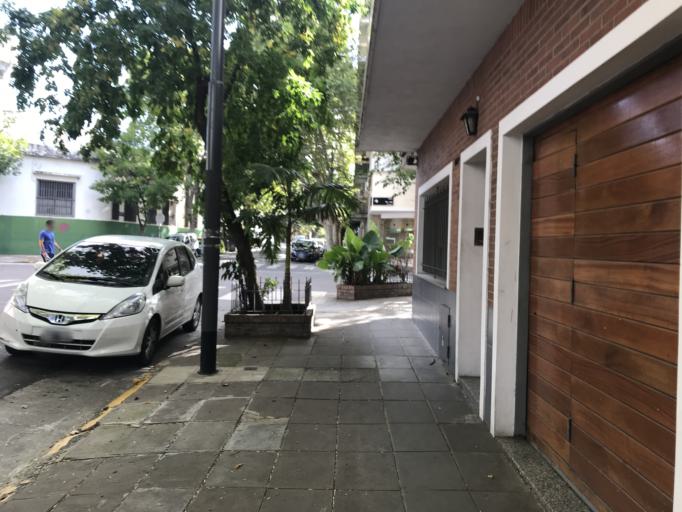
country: AR
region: Buenos Aires F.D.
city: Villa Santa Rita
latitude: -34.6309
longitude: -58.4453
